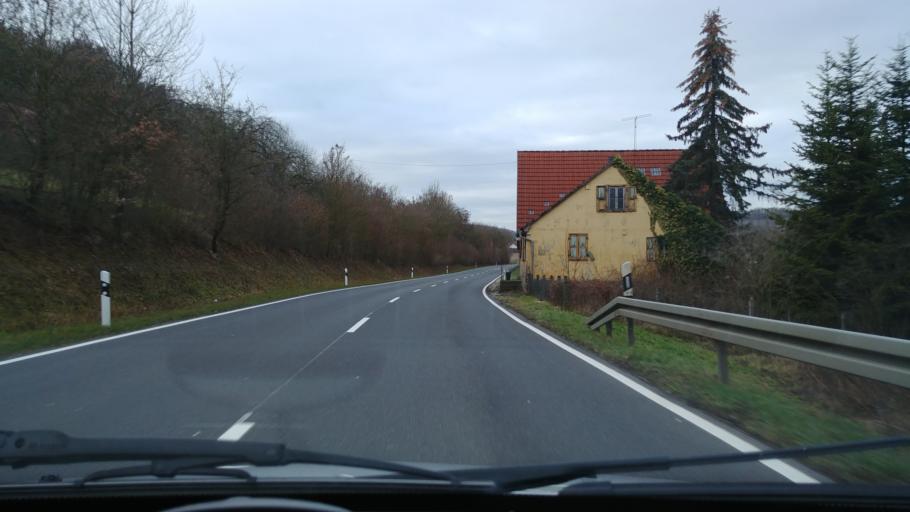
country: DE
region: Bavaria
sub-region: Regierungsbezirk Unterfranken
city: Thungen
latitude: 49.9412
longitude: 9.8418
